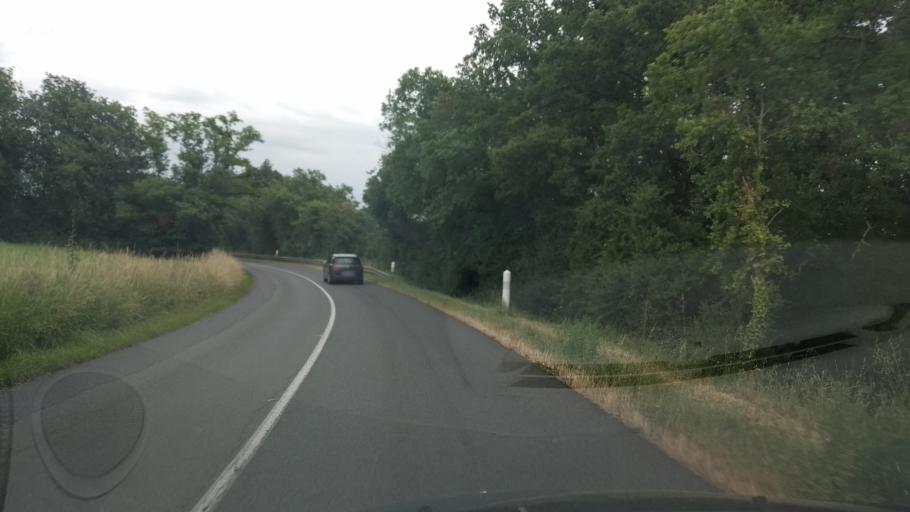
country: FR
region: Poitou-Charentes
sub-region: Departement de la Vienne
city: Biard
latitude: 46.5758
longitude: 0.2970
